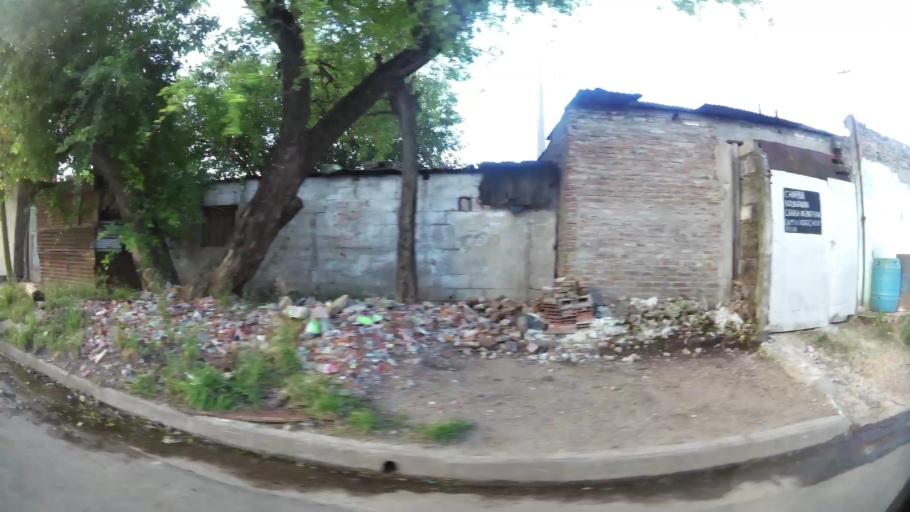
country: AR
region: Santa Fe
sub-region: Departamento de Rosario
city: Rosario
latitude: -32.9820
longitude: -60.6647
